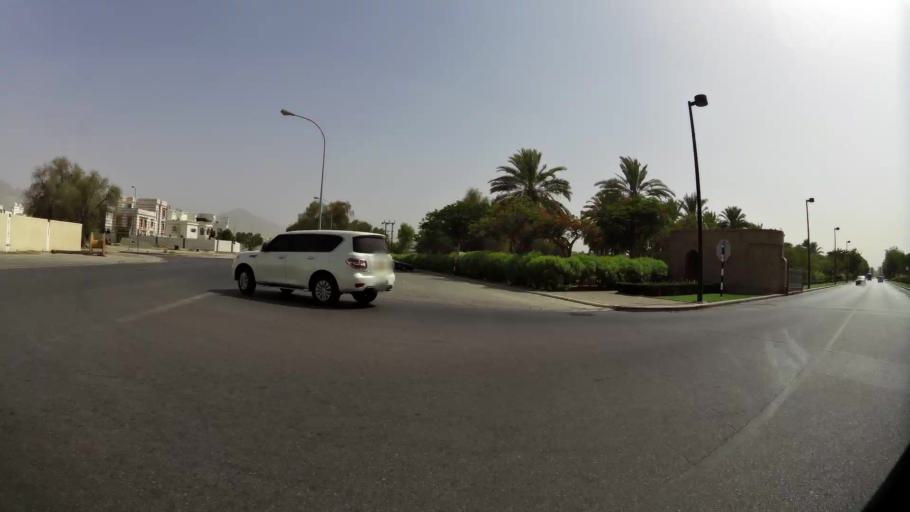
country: OM
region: Muhafazat Masqat
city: Bawshar
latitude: 23.5819
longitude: 58.3920
